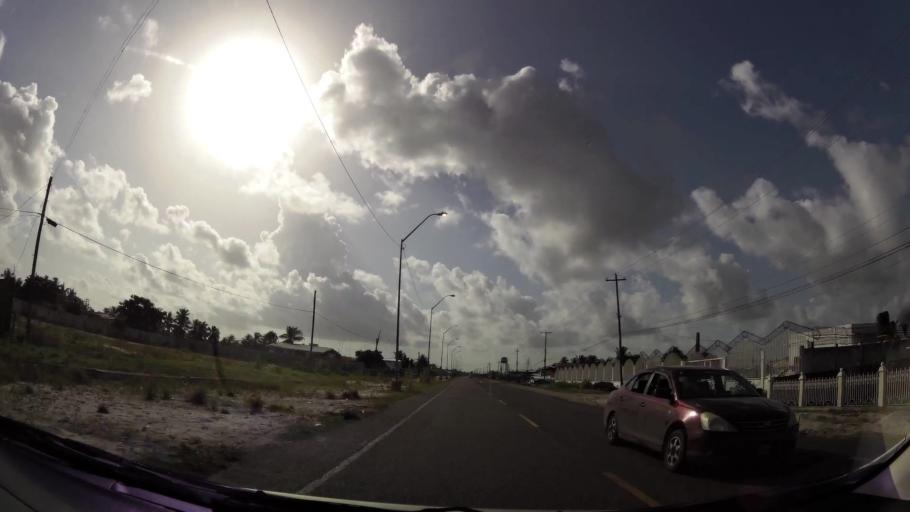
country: GY
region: Demerara-Mahaica
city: Georgetown
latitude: 6.8148
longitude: -58.0699
